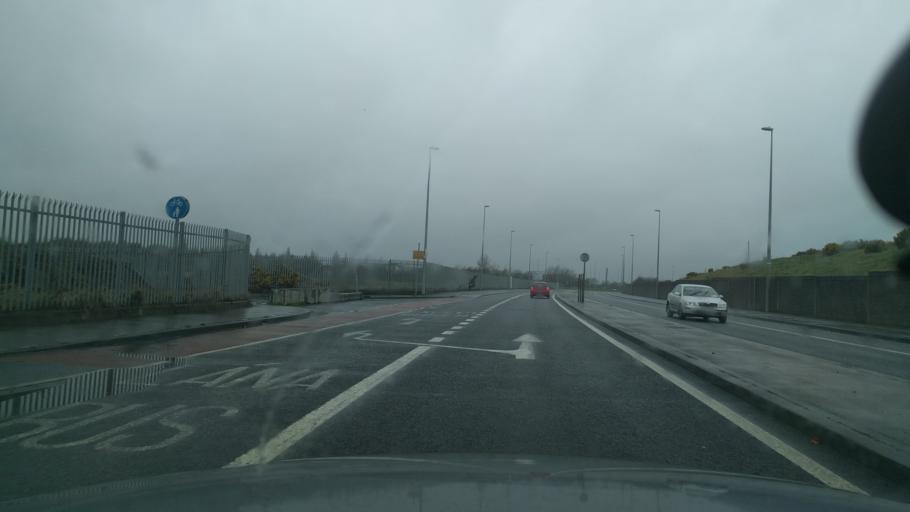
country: IE
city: Jobstown
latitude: 53.2929
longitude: -6.4082
